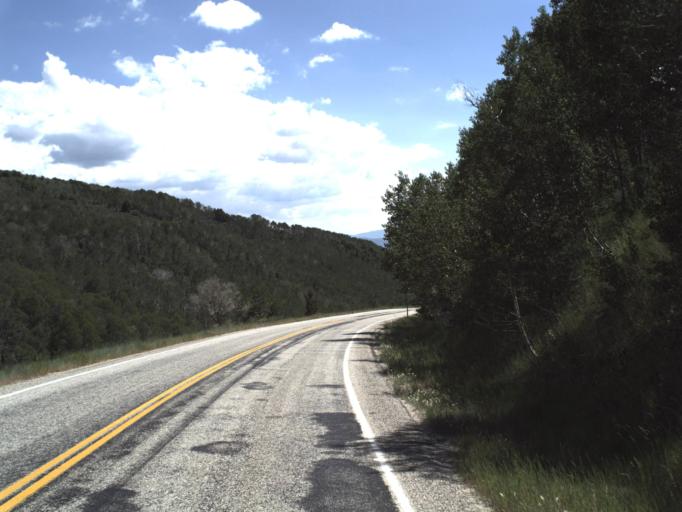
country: US
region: Utah
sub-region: Weber County
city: Wolf Creek
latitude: 41.4180
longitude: -111.5768
